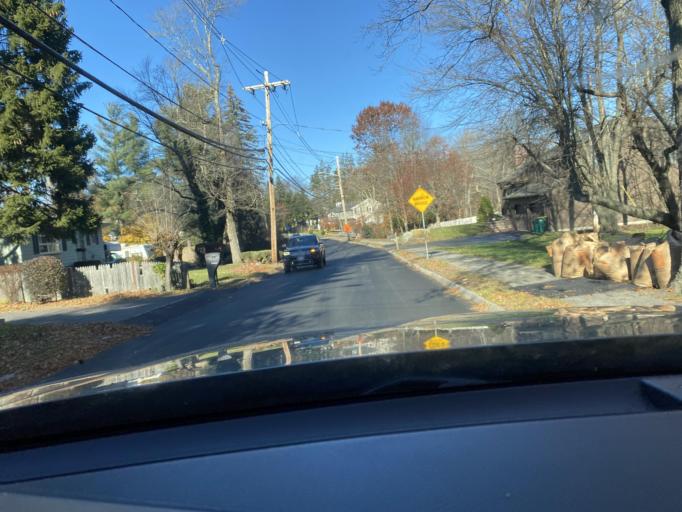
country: US
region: Massachusetts
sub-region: Norfolk County
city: Norwood
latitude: 42.1591
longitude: -71.1954
